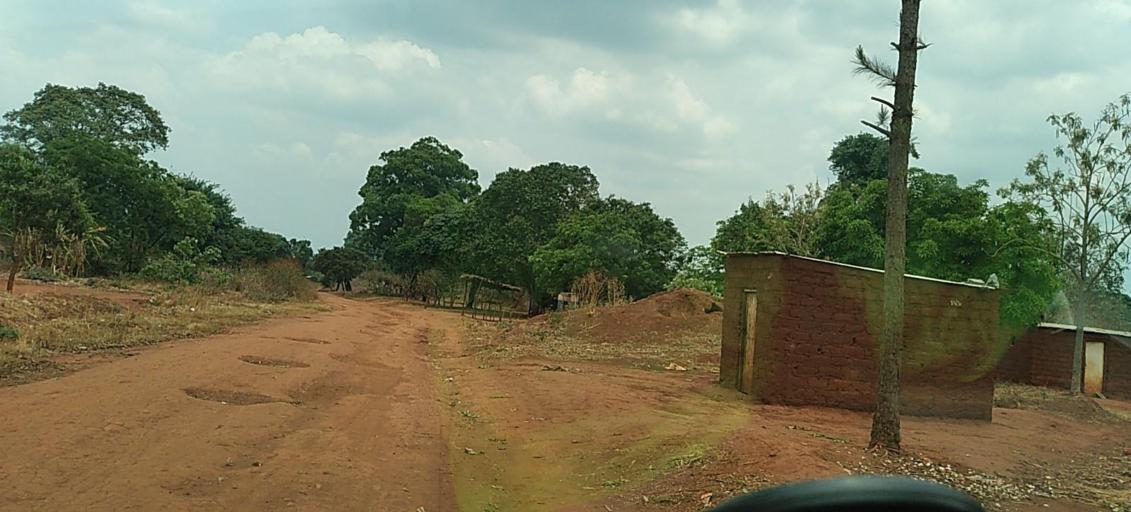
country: ZM
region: North-Western
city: Kansanshi
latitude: -12.0427
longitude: 26.3949
